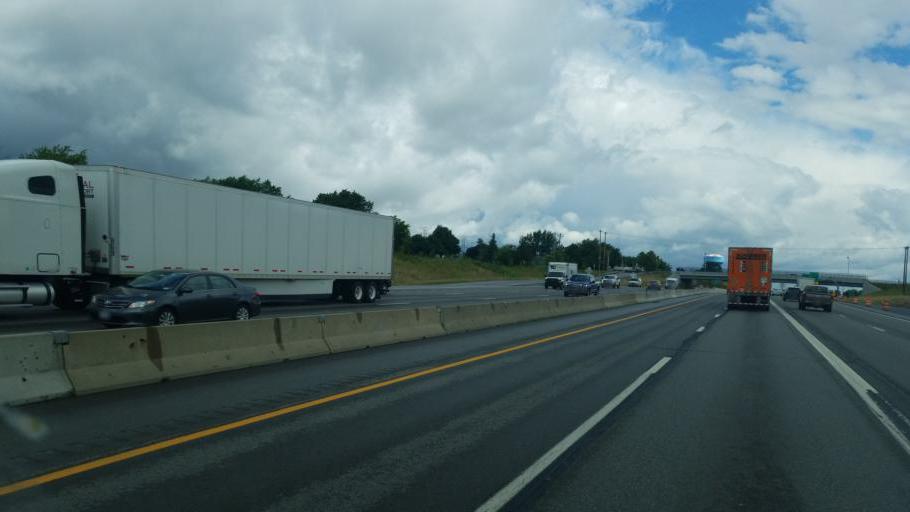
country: US
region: New York
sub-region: Erie County
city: Williamsville
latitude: 42.9425
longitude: -78.7663
